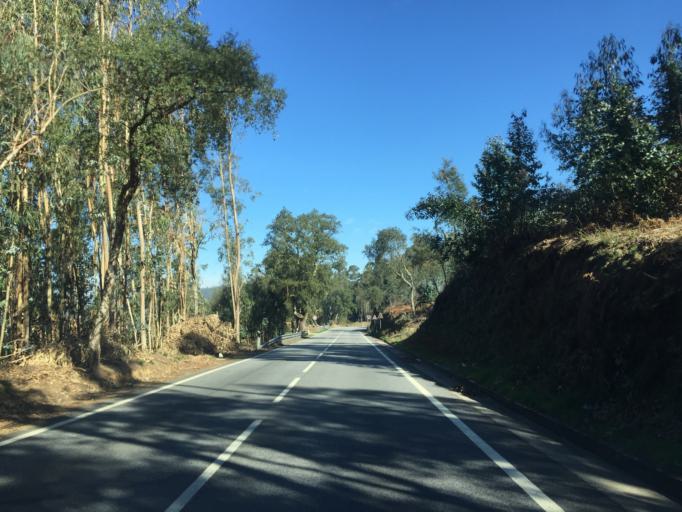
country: PT
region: Aveiro
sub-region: Vale de Cambra
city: Macieira de Cambra
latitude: 40.9010
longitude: -8.3314
